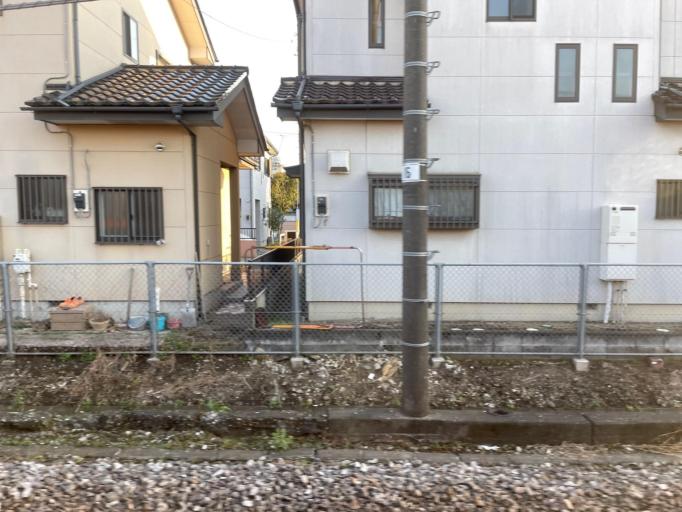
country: JP
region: Gunma
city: Takasaki
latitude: 36.3395
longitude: 138.9990
